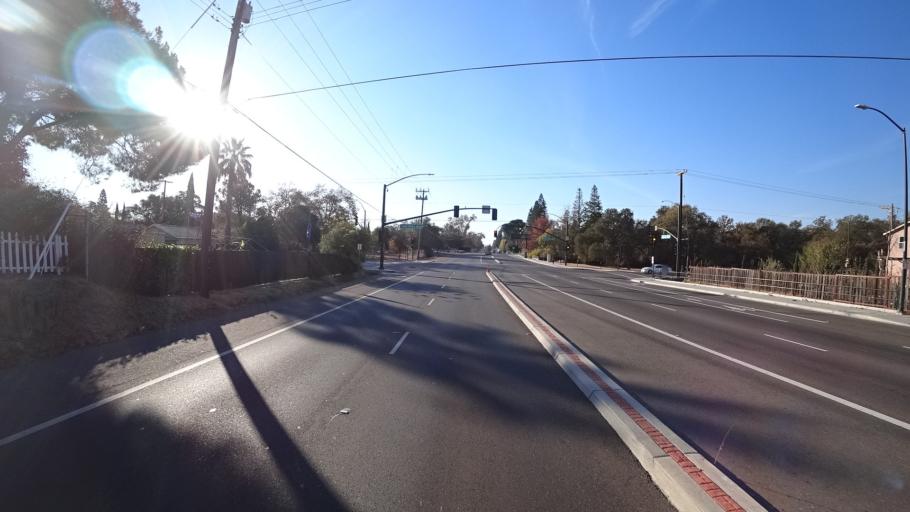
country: US
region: California
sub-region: Sacramento County
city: Citrus Heights
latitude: 38.7192
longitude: -121.2718
